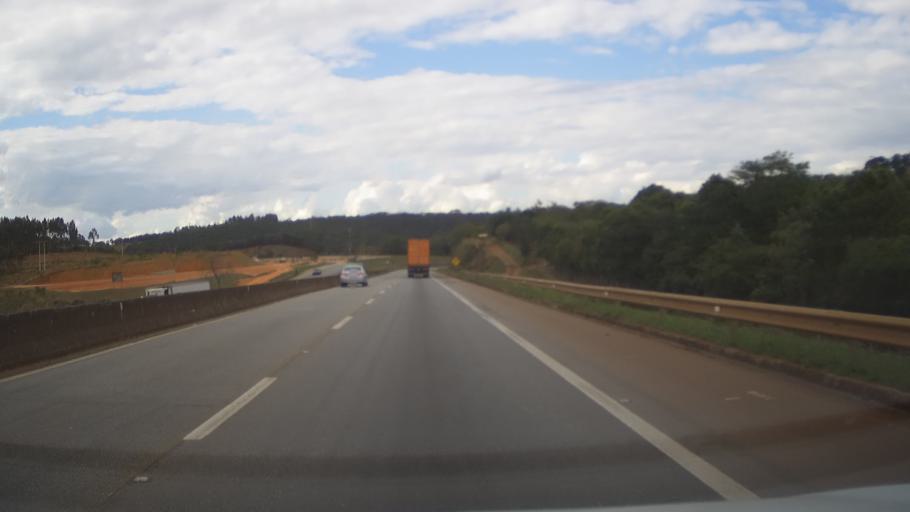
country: BR
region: Minas Gerais
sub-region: Itauna
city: Itauna
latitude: -20.2894
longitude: -44.4359
